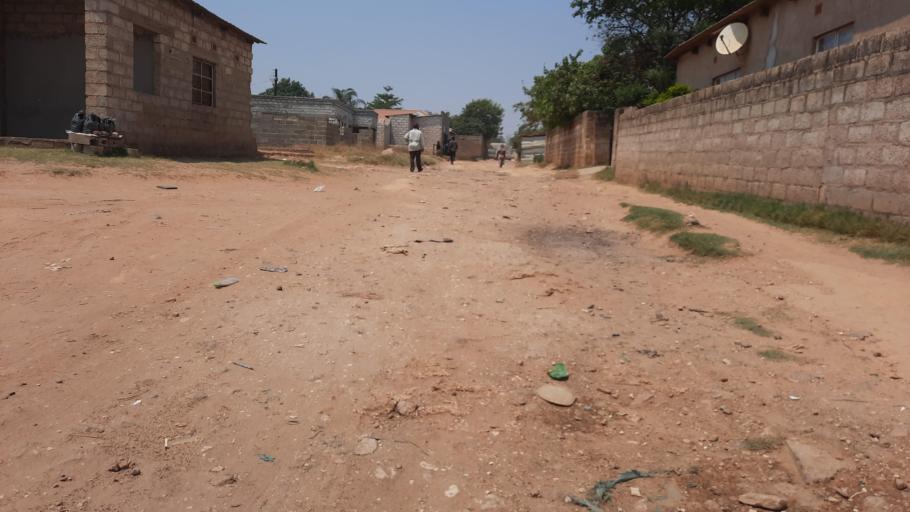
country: ZM
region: Lusaka
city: Lusaka
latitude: -15.4054
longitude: 28.3810
